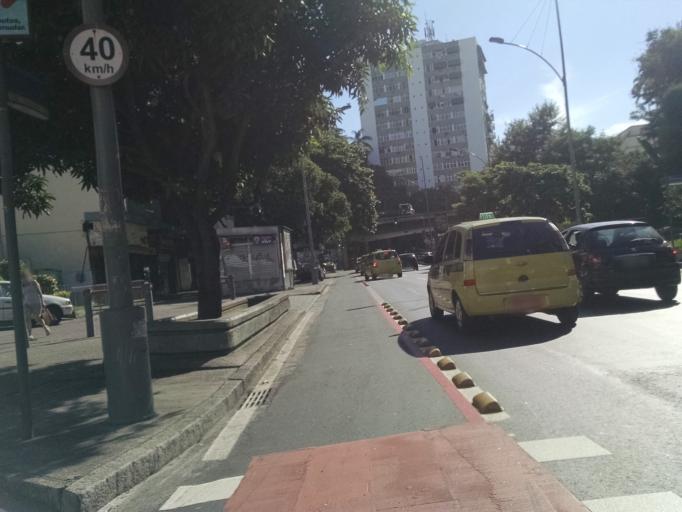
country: BR
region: Rio de Janeiro
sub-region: Rio De Janeiro
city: Rio de Janeiro
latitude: -22.9329
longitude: -43.1838
